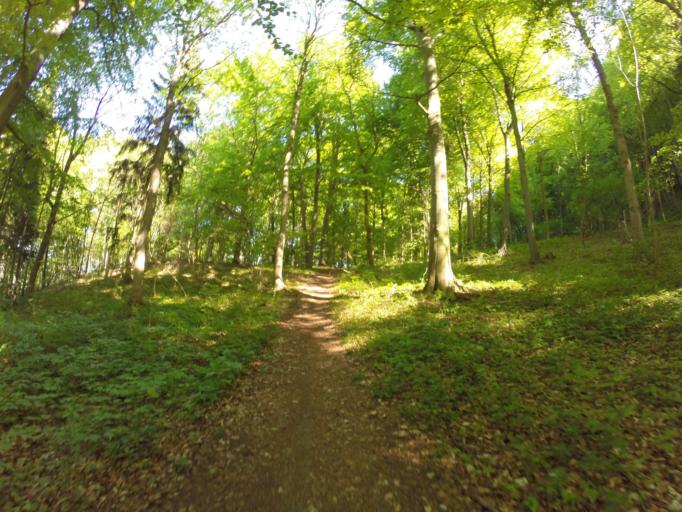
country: DE
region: Thuringia
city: Golmsdorf
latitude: 50.9434
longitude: 11.6358
